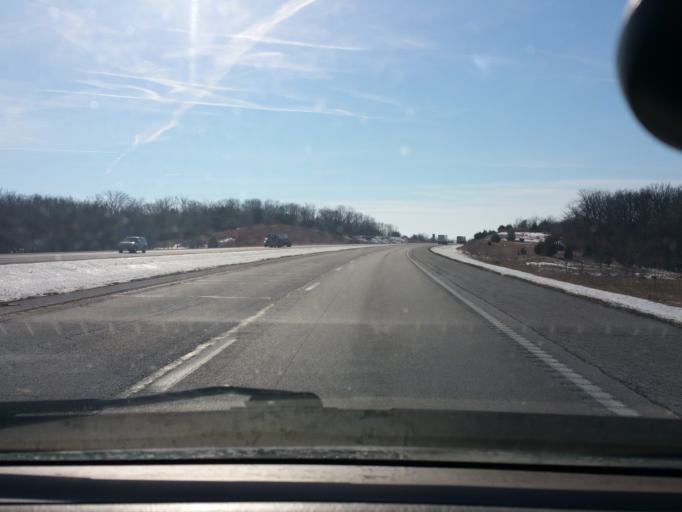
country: US
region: Missouri
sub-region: Harrison County
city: Bethany
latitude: 40.1823
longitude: -94.0150
